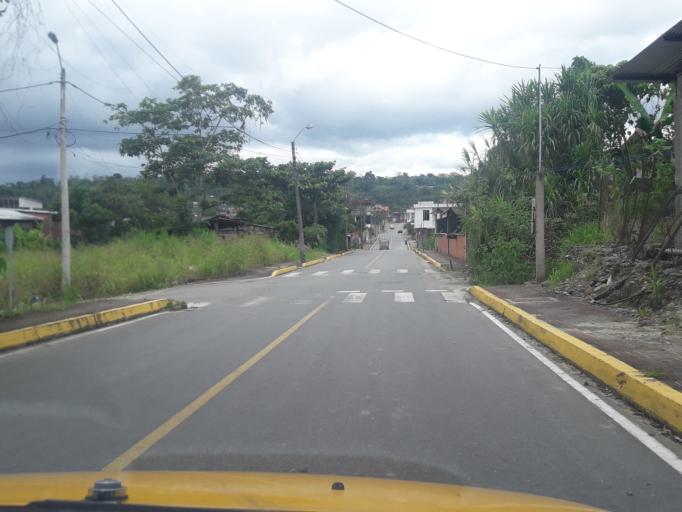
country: EC
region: Napo
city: Tena
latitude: -1.0048
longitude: -77.8175
